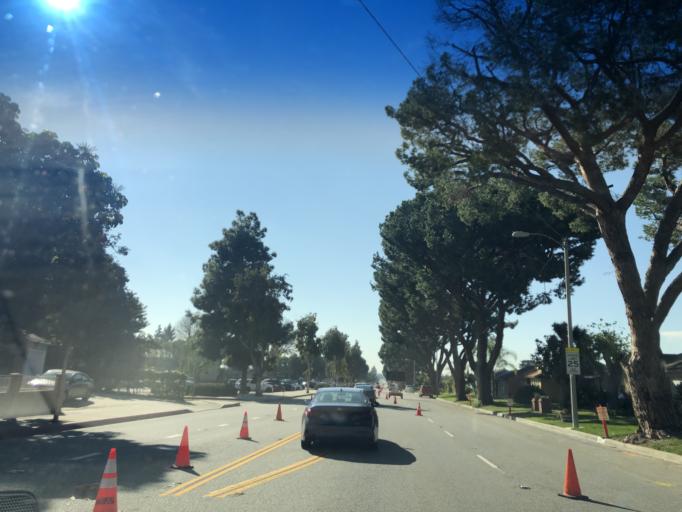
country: US
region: California
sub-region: Los Angeles County
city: South Whittier
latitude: 33.9457
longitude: -118.0214
